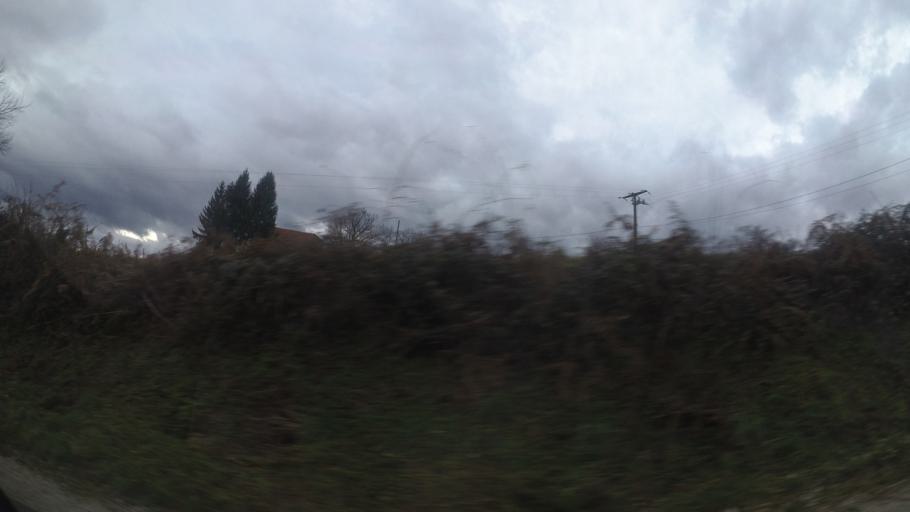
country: HR
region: Karlovacka
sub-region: Grad Karlovac
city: Karlovac
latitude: 45.3874
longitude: 15.5389
